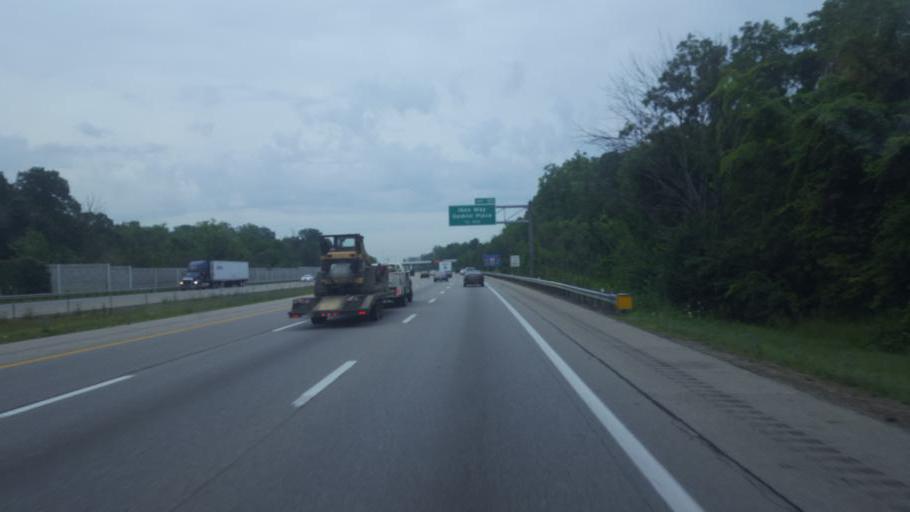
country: US
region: Ohio
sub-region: Franklin County
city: Westerville
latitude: 40.1597
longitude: -82.9685
